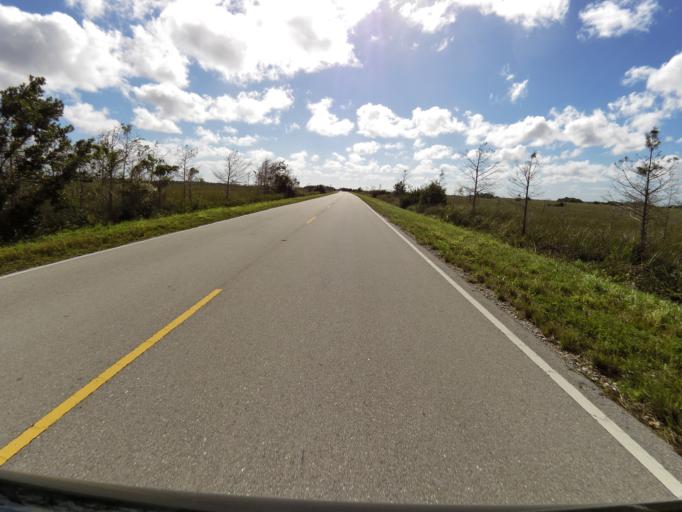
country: US
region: Florida
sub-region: Miami-Dade County
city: Florida City
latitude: 25.3695
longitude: -80.8174
